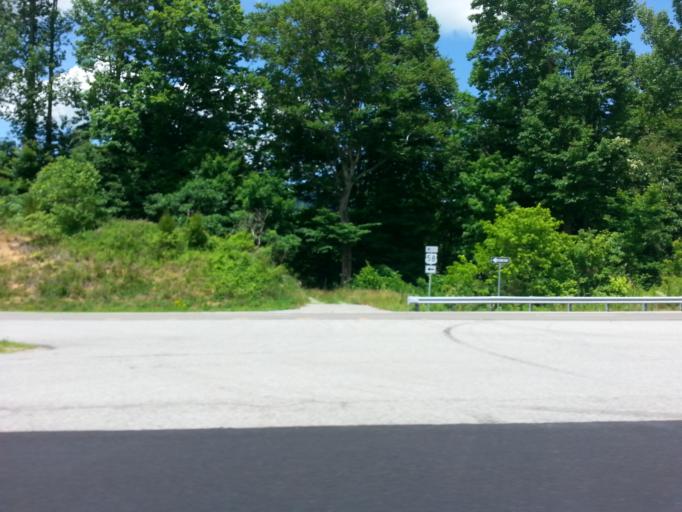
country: US
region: Virginia
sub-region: Lee County
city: Jonesville
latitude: 36.6979
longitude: -83.2530
